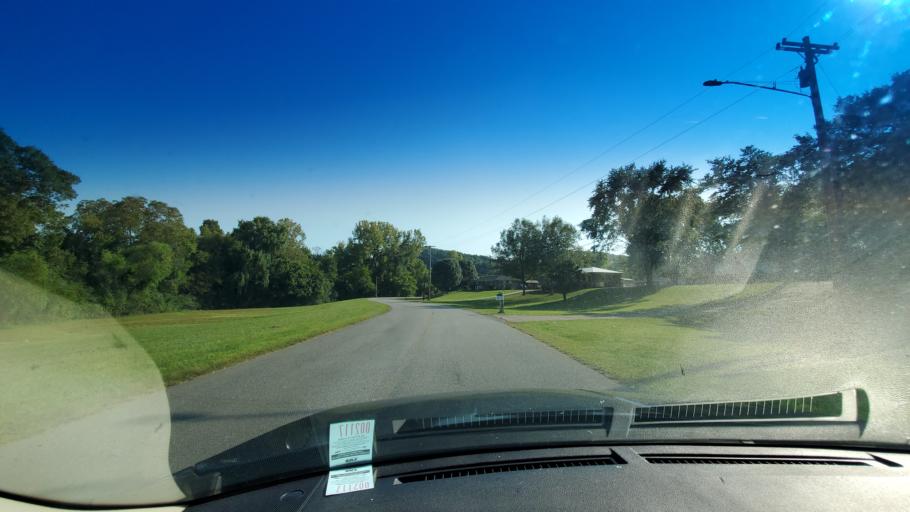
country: US
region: Tennessee
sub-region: Smith County
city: Carthage
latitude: 36.2568
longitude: -85.9561
